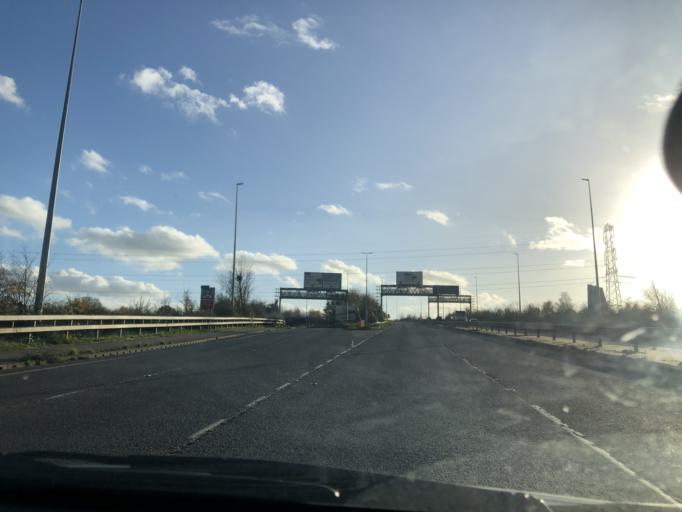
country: GB
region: England
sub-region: Kent
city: Greenhithe
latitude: 51.4365
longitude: 0.2785
